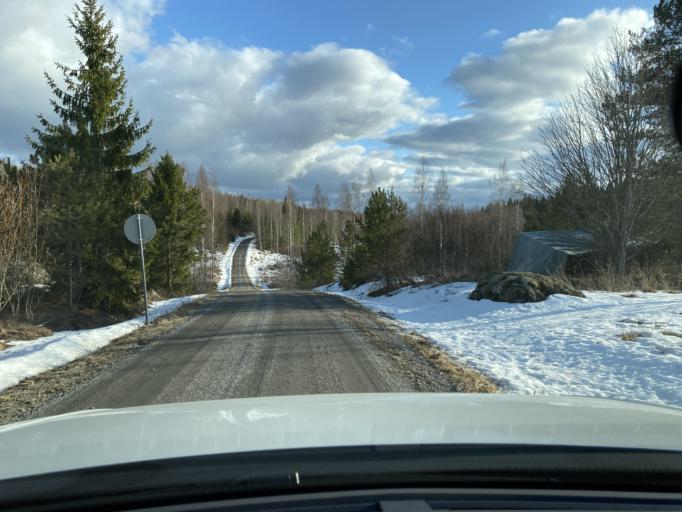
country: FI
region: Pirkanmaa
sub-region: Lounais-Pirkanmaa
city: Mouhijaervi
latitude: 61.4575
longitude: 22.9586
